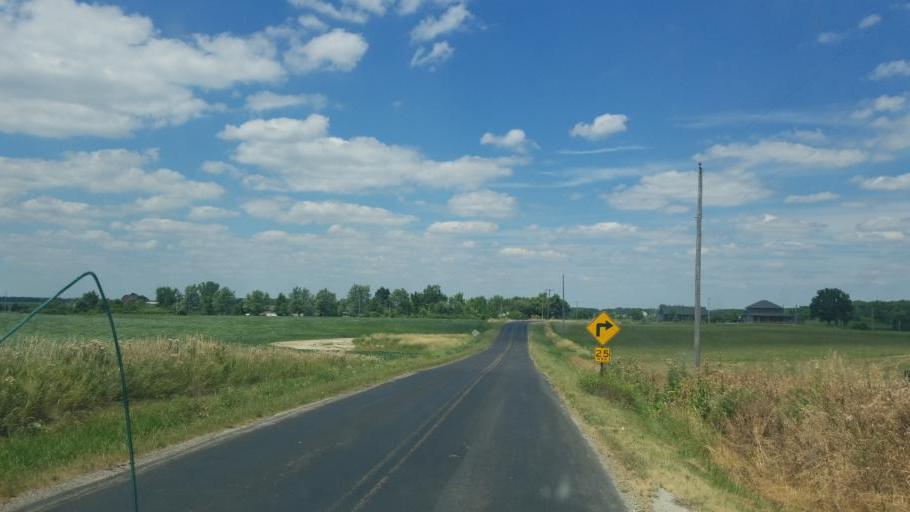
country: US
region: Ohio
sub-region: Williams County
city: Edgerton
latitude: 41.4636
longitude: -84.7104
